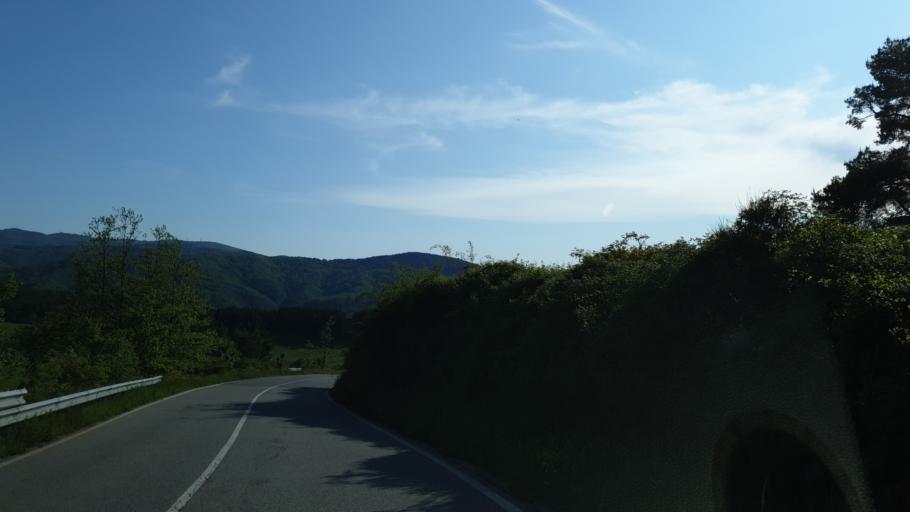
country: IT
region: Tuscany
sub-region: Province of Arezzo
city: Montemignaio
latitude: 43.7877
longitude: 11.6267
